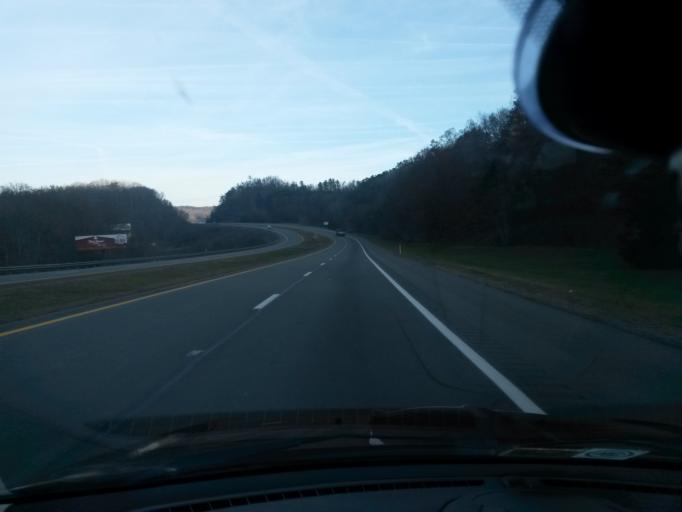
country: US
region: West Virginia
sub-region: Greenbrier County
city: Lewisburg
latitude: 37.7786
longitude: -80.3818
